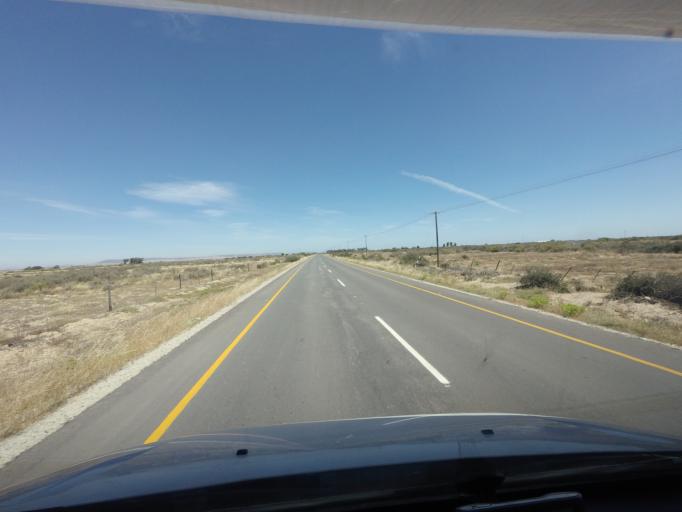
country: ZA
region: Western Cape
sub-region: West Coast District Municipality
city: Vredenburg
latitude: -32.7928
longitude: 18.2277
